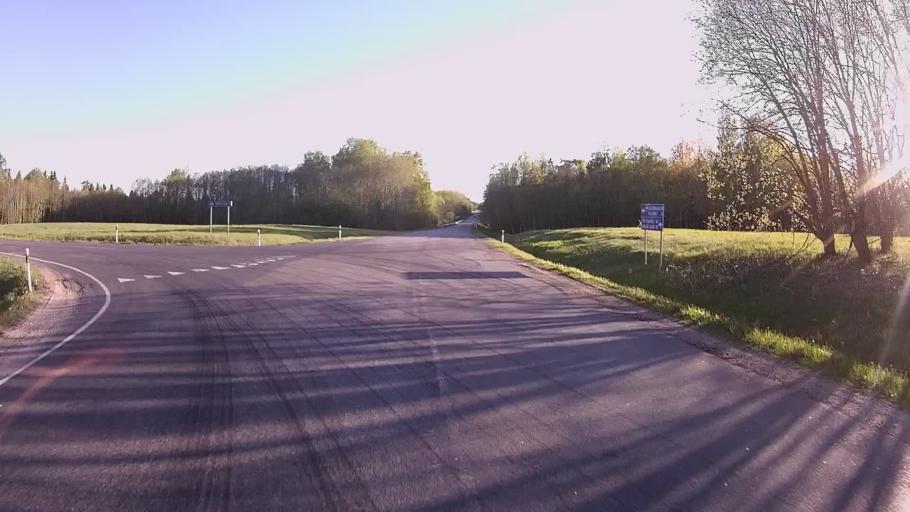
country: EE
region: Viljandimaa
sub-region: Viiratsi vald
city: Viiratsi
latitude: 58.4210
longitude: 25.7020
